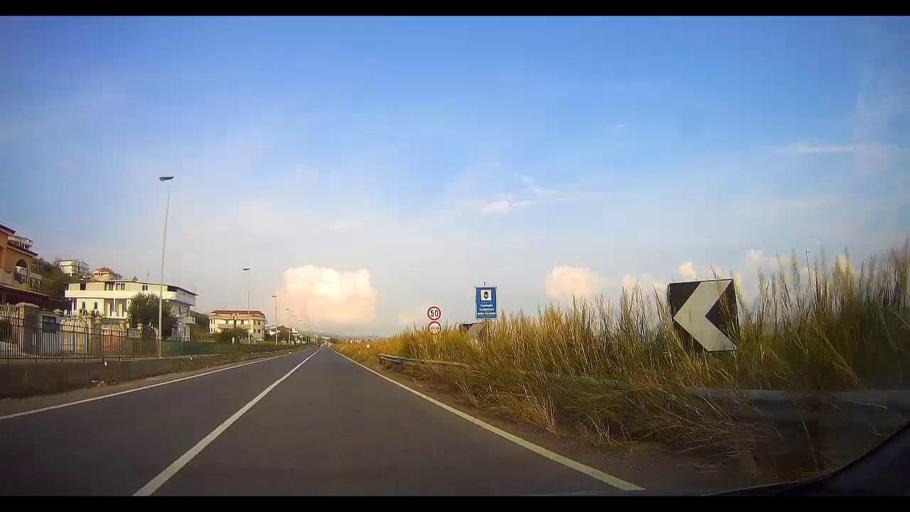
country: IT
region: Calabria
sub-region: Provincia di Cosenza
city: Cariati
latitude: 39.5277
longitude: 16.8871
